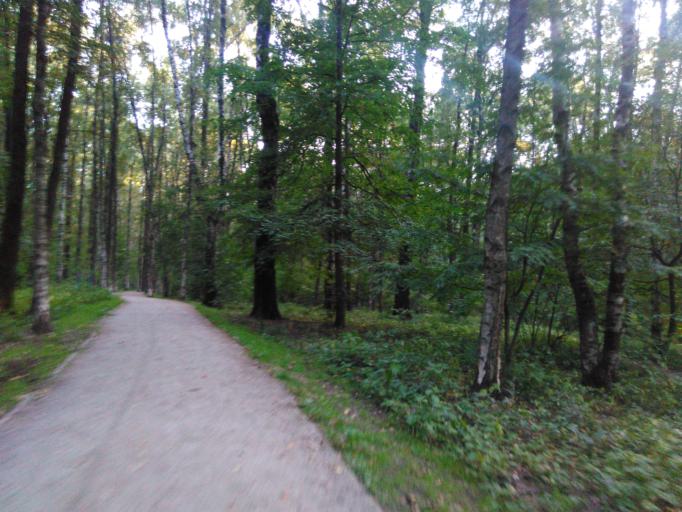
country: RU
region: Moscow
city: Troparevo
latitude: 55.6583
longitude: 37.5052
